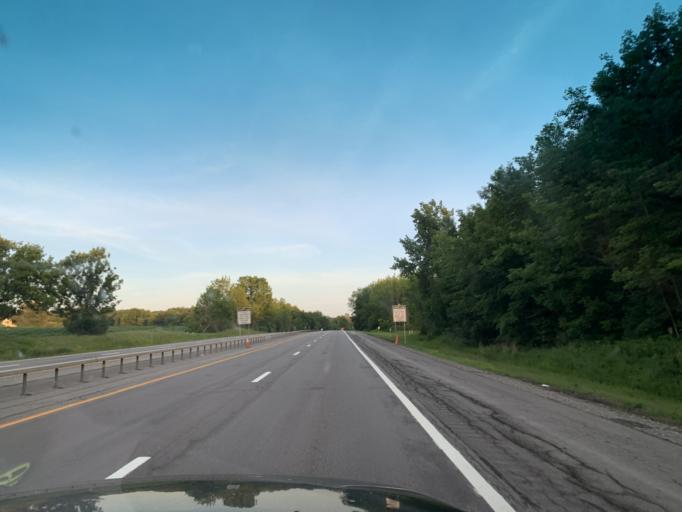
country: US
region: New York
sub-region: Oneida County
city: Chadwicks
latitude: 43.0193
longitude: -75.2583
